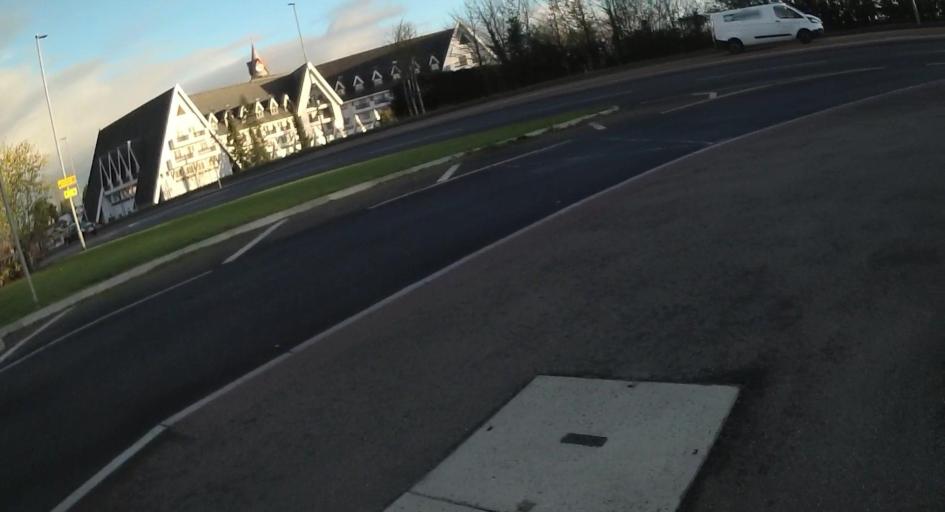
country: GB
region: England
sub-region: Bracknell Forest
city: Binfield
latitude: 51.4154
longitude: -0.7920
